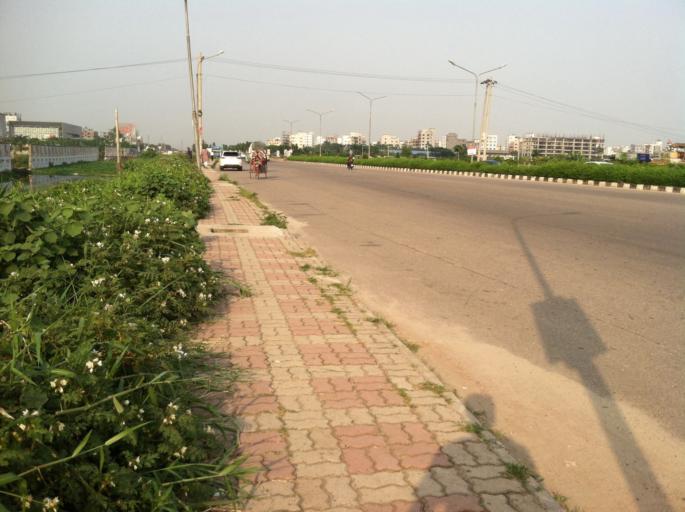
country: BD
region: Dhaka
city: Tungi
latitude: 23.8257
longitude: 90.4239
